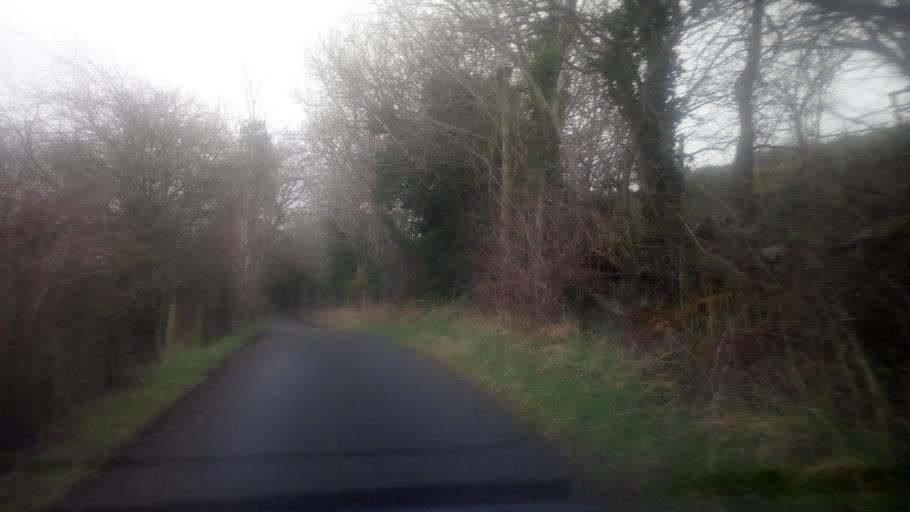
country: GB
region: Scotland
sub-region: The Scottish Borders
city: Jedburgh
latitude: 55.4904
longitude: -2.5414
